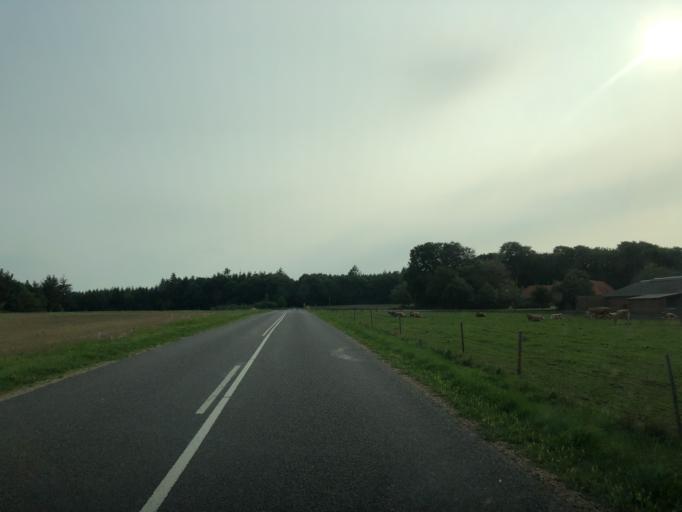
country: DK
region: Central Jutland
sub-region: Ringkobing-Skjern Kommune
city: Videbaek
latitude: 56.0667
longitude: 8.6921
